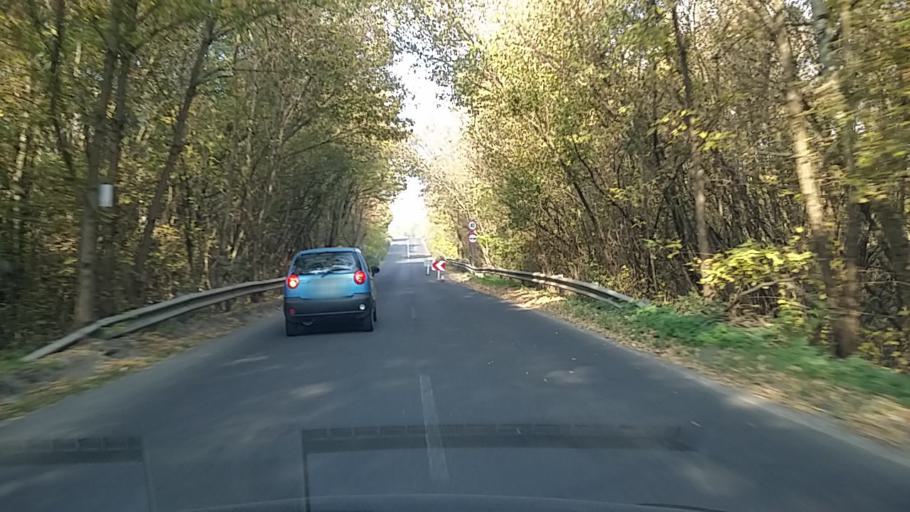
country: HU
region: Pest
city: Fot
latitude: 47.5987
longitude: 19.1538
